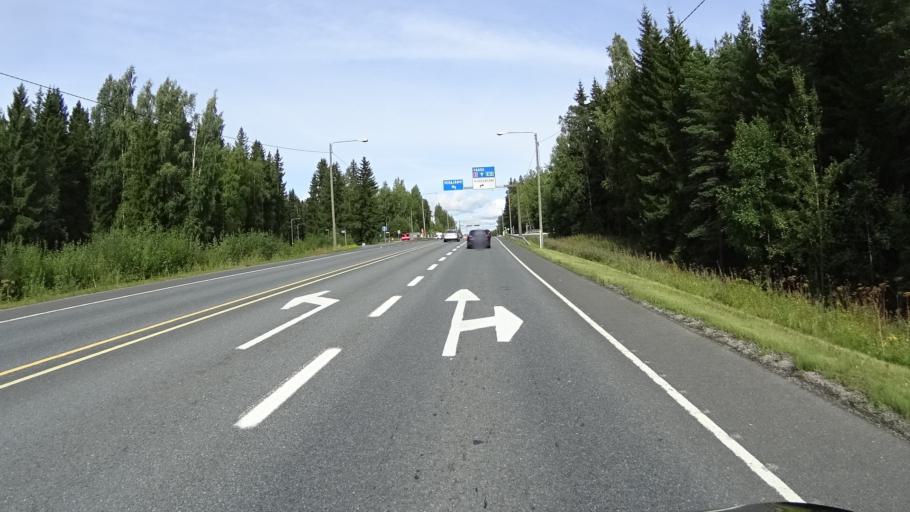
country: FI
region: Pirkanmaa
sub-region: Tampere
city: Haemeenkyroe
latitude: 61.6746
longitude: 23.1597
